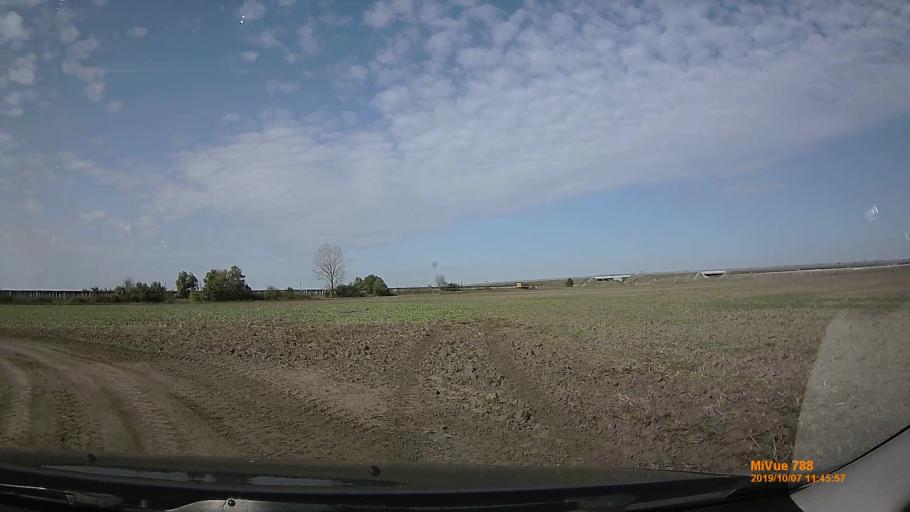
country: HU
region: Bekes
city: Nagyszenas
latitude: 46.8076
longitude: 20.6787
